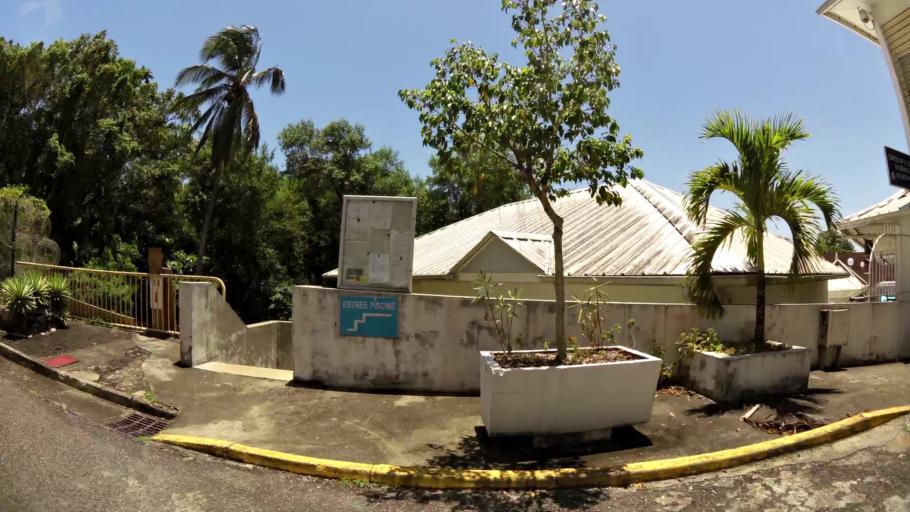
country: GF
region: Guyane
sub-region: Guyane
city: Cayenne
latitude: 4.9390
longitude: -52.3371
